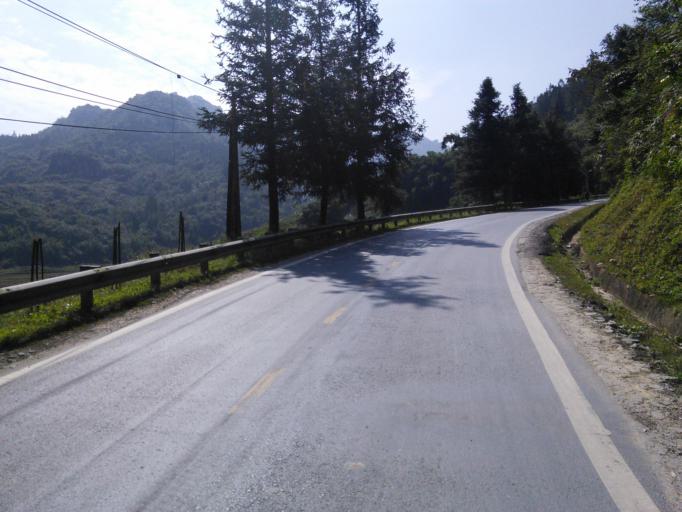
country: VN
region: Lao Cai
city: Sa Pa
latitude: 22.3593
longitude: 103.8636
